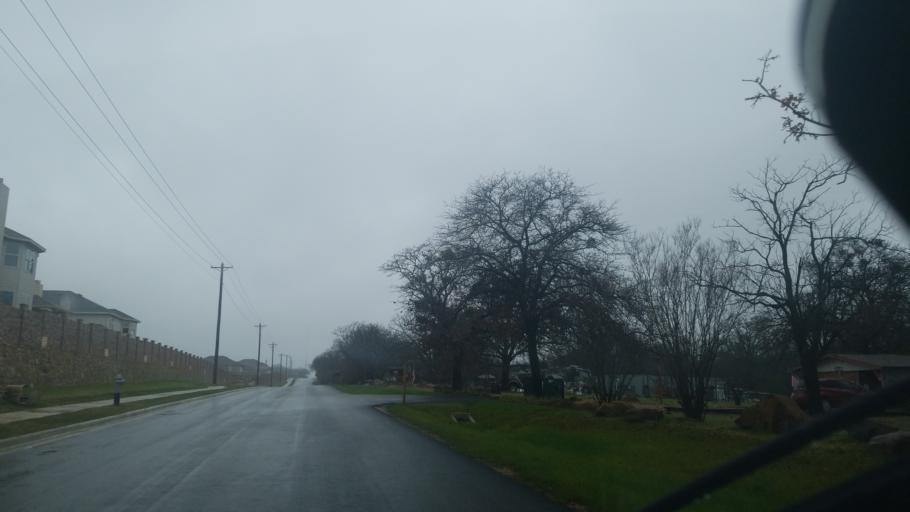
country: US
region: Texas
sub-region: Denton County
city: Corinth
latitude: 33.1779
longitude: -97.0695
